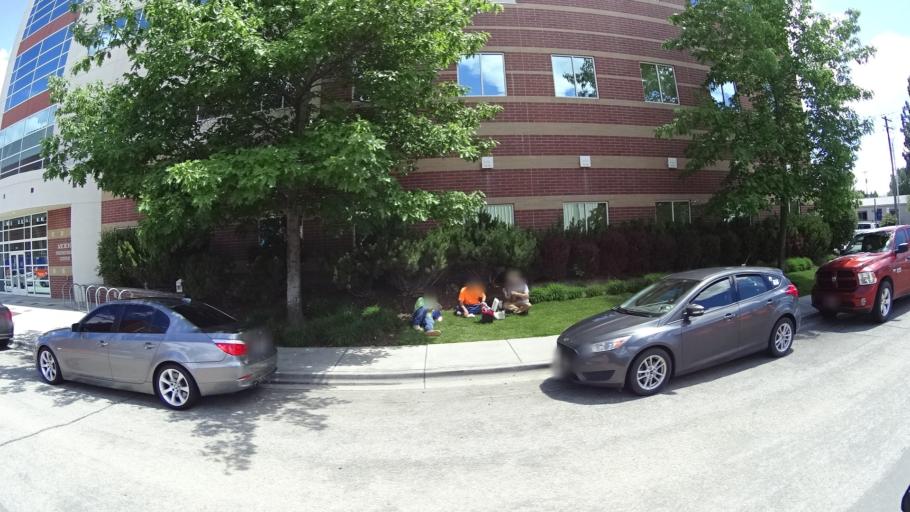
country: US
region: Idaho
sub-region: Ada County
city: Boise
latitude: 43.6000
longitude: -116.1986
